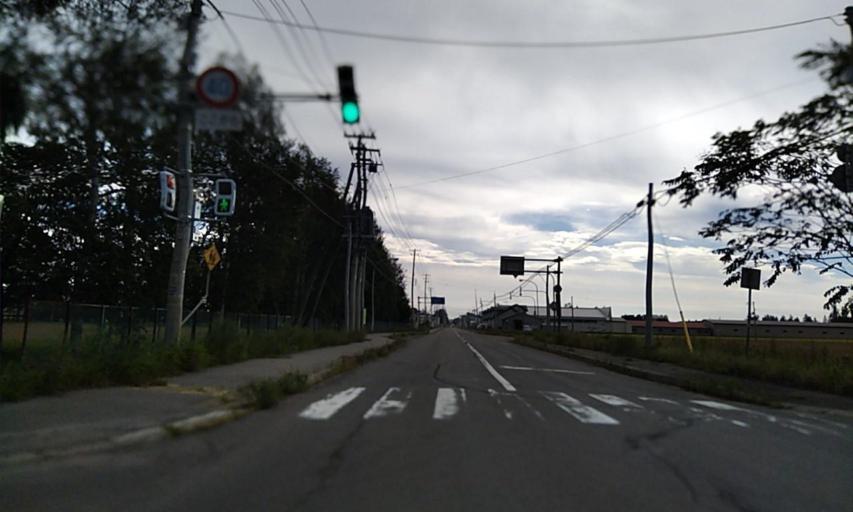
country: JP
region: Hokkaido
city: Obihiro
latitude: 42.8512
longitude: 143.1615
